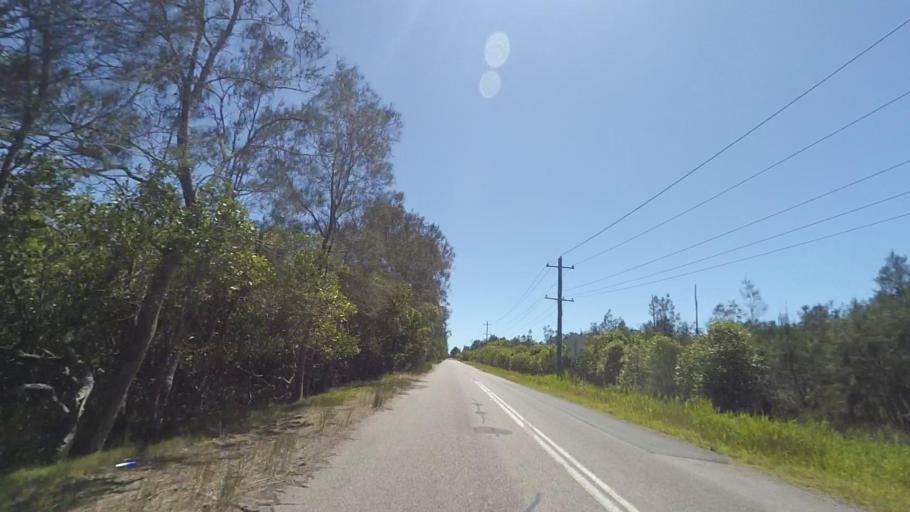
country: AU
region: New South Wales
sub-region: Port Stephens Shire
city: Medowie
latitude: -32.7861
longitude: 151.9369
